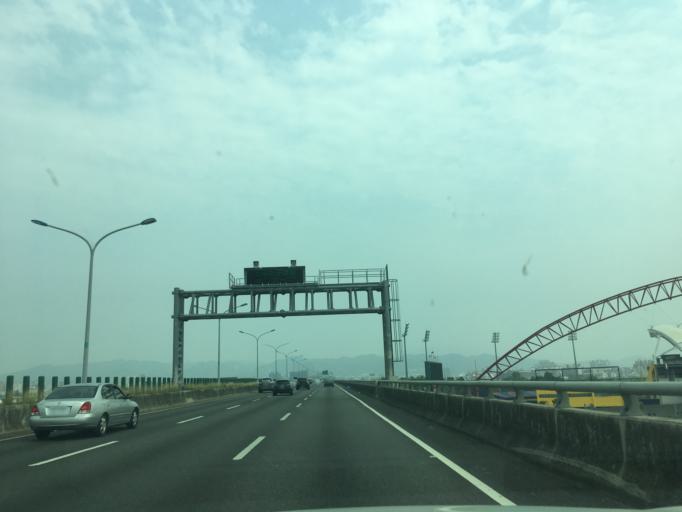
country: TW
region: Taiwan
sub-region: Taichung City
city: Taichung
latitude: 24.2010
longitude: 120.6818
